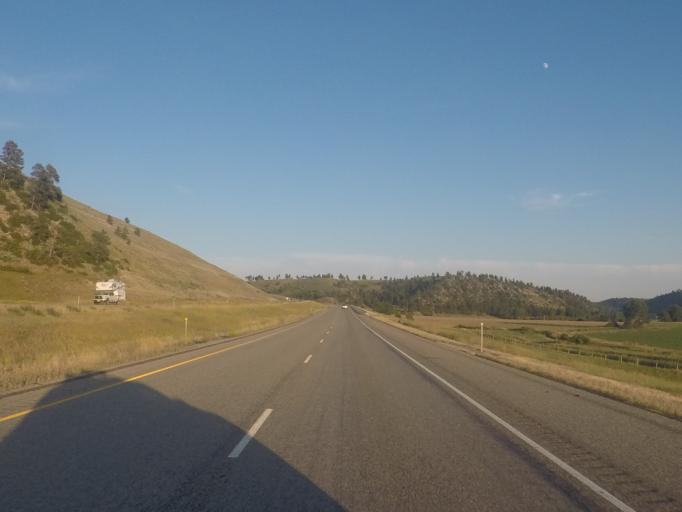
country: US
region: Montana
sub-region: Stillwater County
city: Columbus
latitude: 45.6660
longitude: -109.3372
